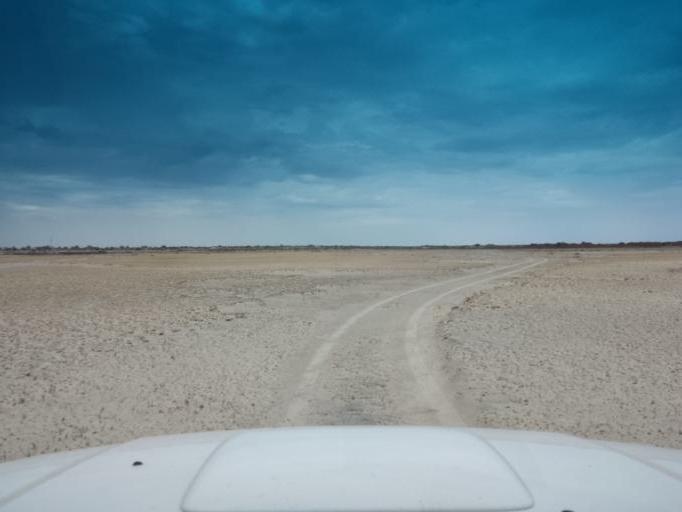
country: BW
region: Central
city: Mopipi
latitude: -21.1845
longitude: 24.8662
